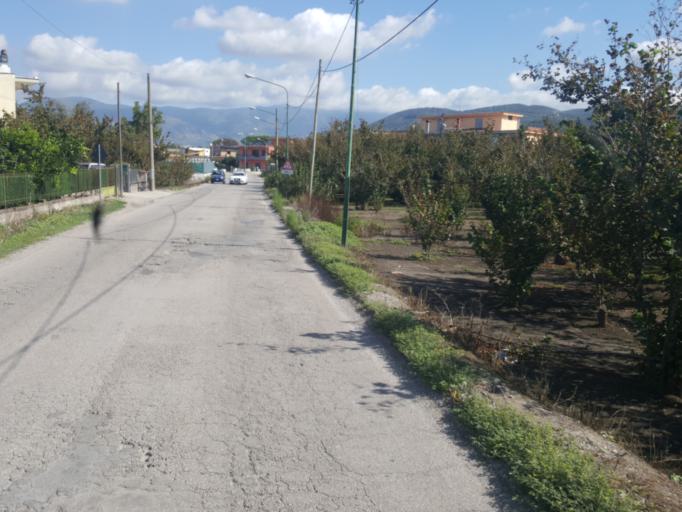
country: IT
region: Campania
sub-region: Provincia di Napoli
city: Piazzolla
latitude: 40.9036
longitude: 14.5275
